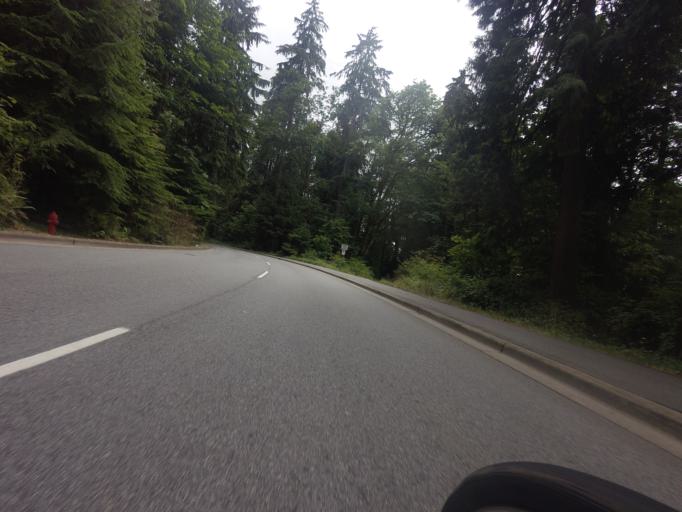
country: CA
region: British Columbia
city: West End
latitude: 49.3083
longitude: -123.1530
